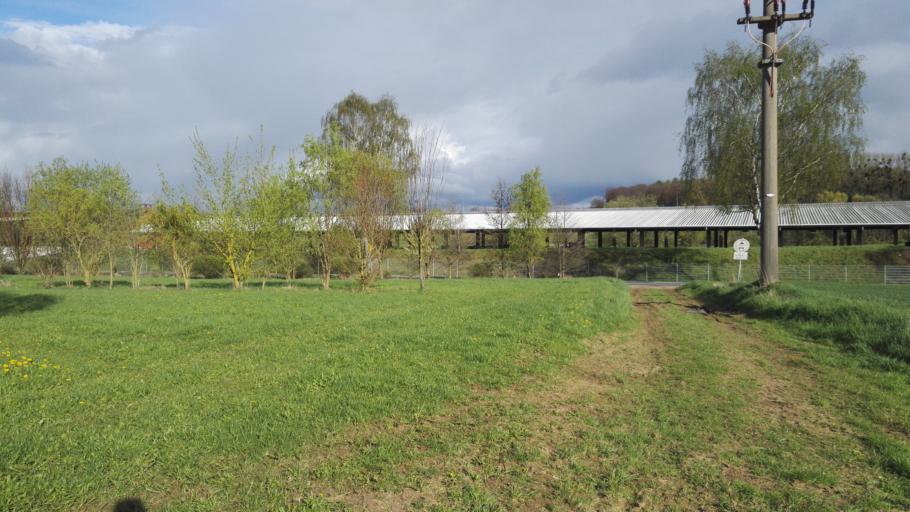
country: DE
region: Lower Saxony
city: Holle
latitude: 52.0704
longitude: 10.1365
